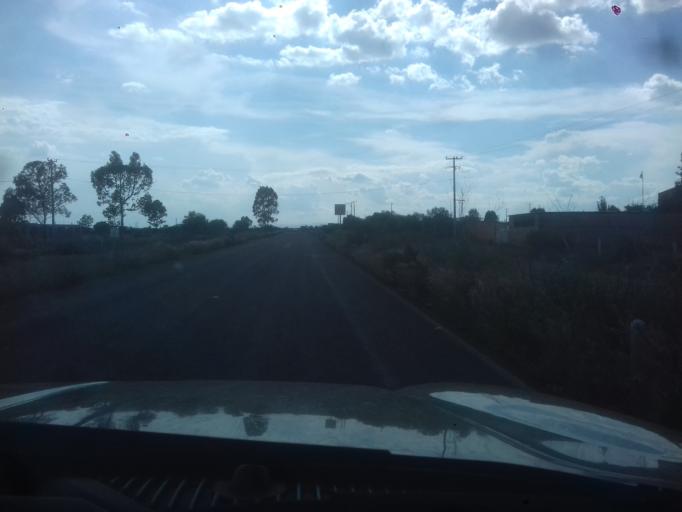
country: MX
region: Aguascalientes
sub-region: Aguascalientes
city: Villa Licenciado Jesus Teran (Calvillito)
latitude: 21.7941
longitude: -102.2195
